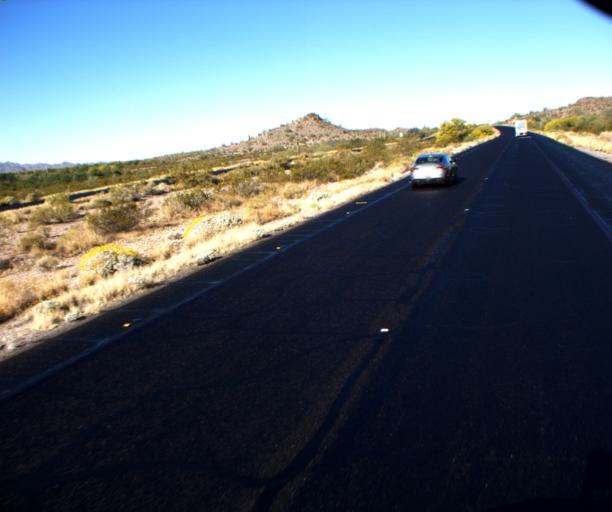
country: US
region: Arizona
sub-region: Pinal County
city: Maricopa
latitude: 32.8484
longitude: -112.3072
